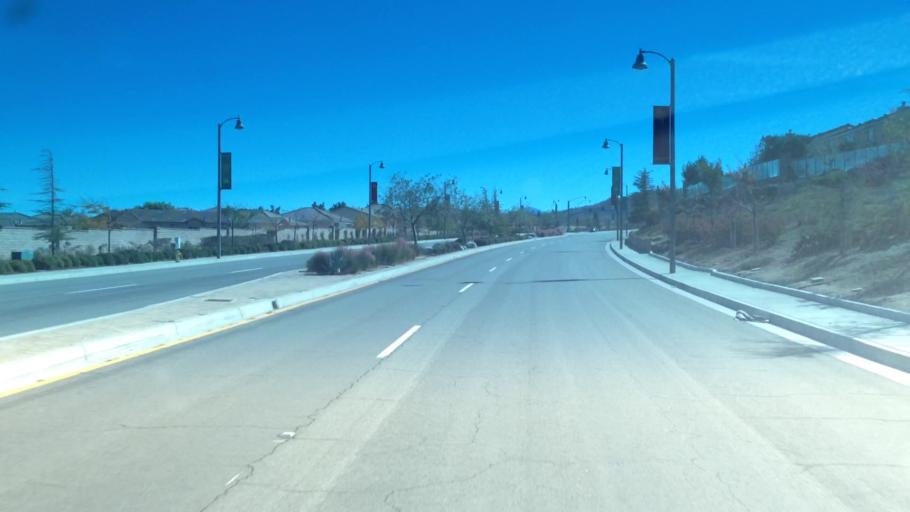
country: US
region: California
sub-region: Los Angeles County
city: Desert View Highlands
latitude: 34.5637
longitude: -118.1715
